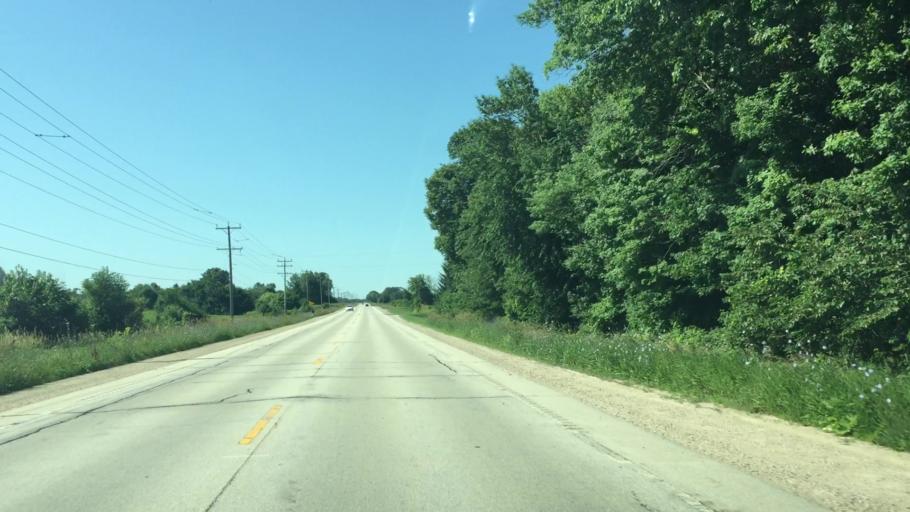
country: US
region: Wisconsin
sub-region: Calumet County
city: Sherwood
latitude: 44.1542
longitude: -88.2648
